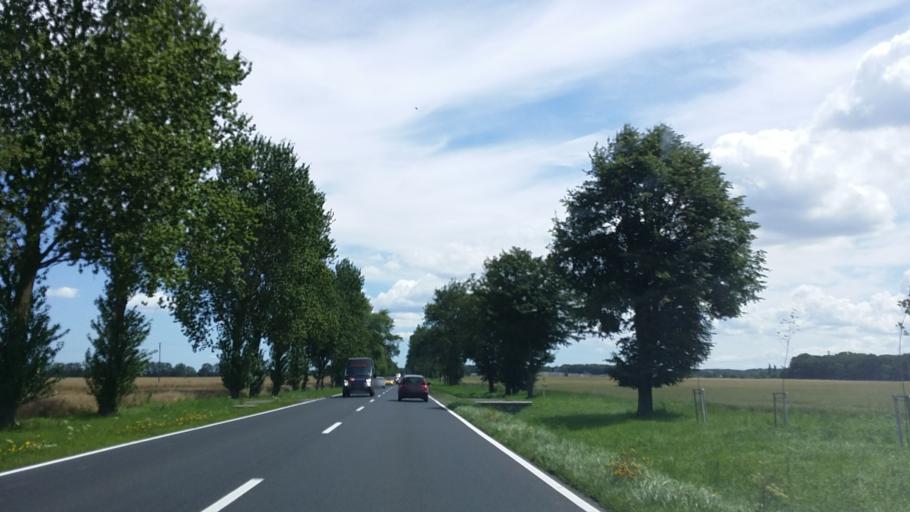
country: PL
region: West Pomeranian Voivodeship
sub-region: Powiat koszalinski
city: Mielno
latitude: 54.2227
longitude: 16.0559
